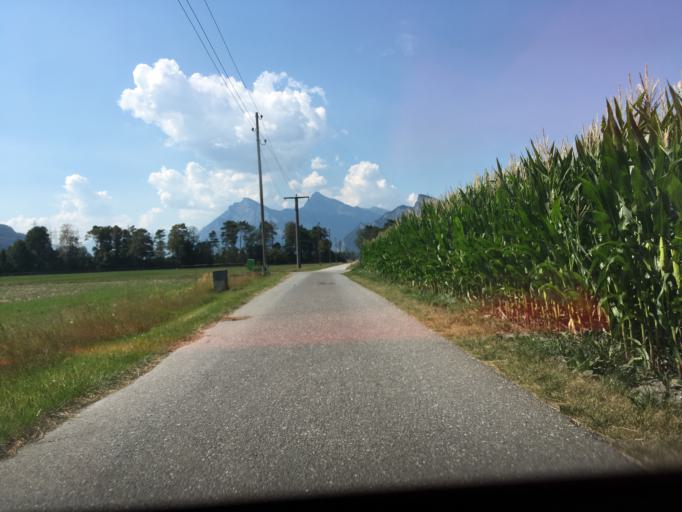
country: CH
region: Grisons
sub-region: Landquart District
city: Maienfeld
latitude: 46.9868
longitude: 9.5413
